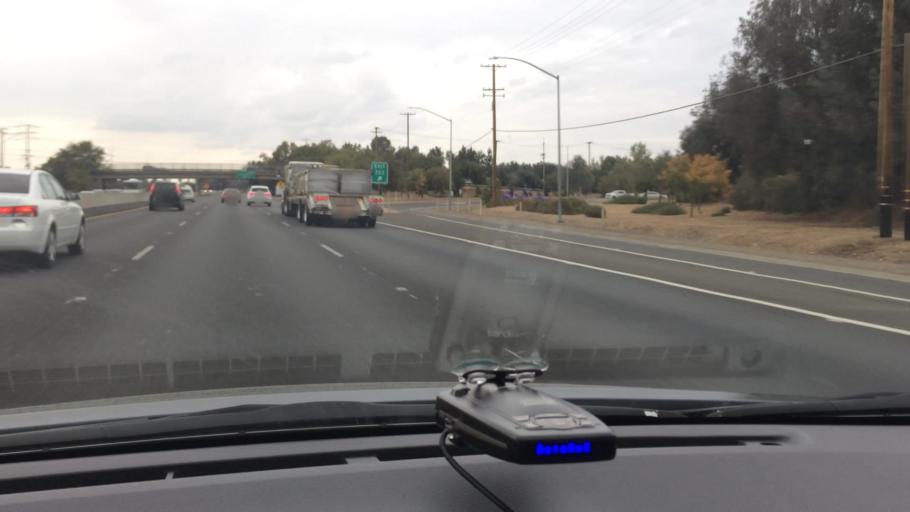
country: US
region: California
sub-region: San Joaquin County
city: Lodi
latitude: 38.0994
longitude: -121.2601
